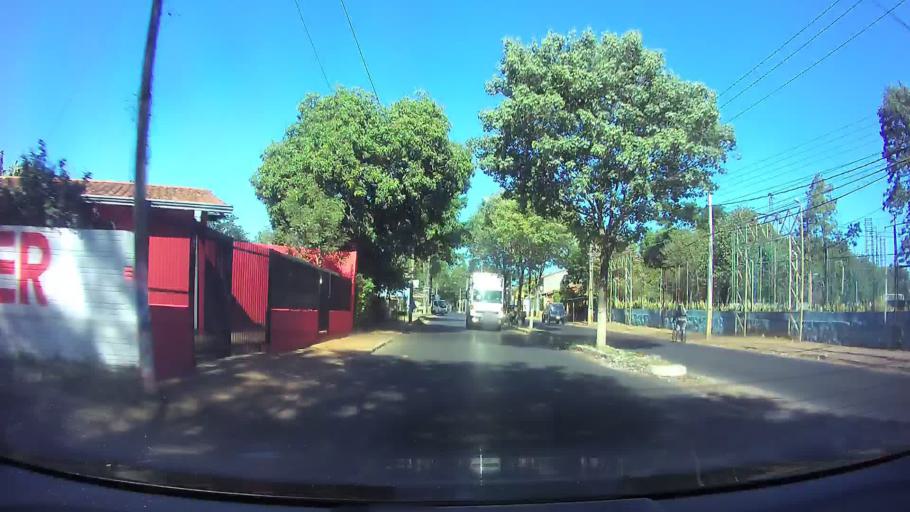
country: PY
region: Central
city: Villa Elisa
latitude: -25.3703
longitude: -57.5786
